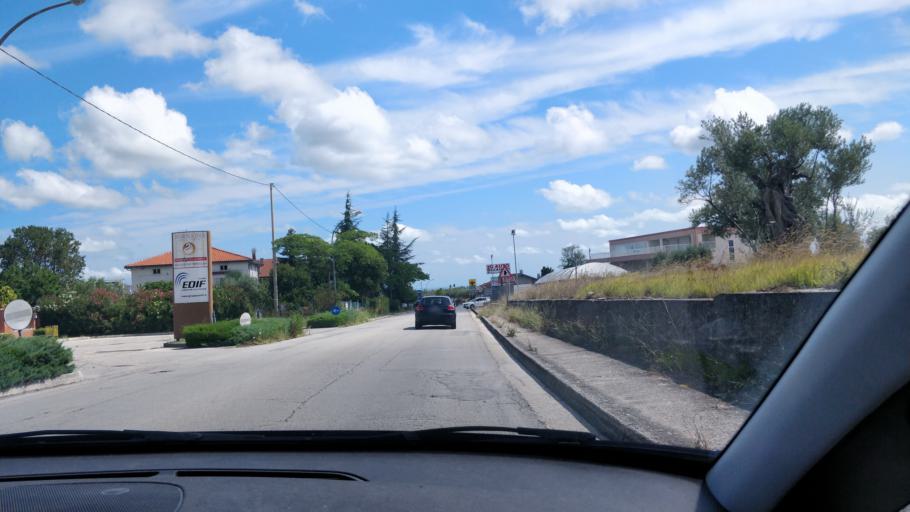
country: IT
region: Abruzzo
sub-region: Provincia di Chieti
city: Treglio
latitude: 42.2457
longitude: 14.4165
